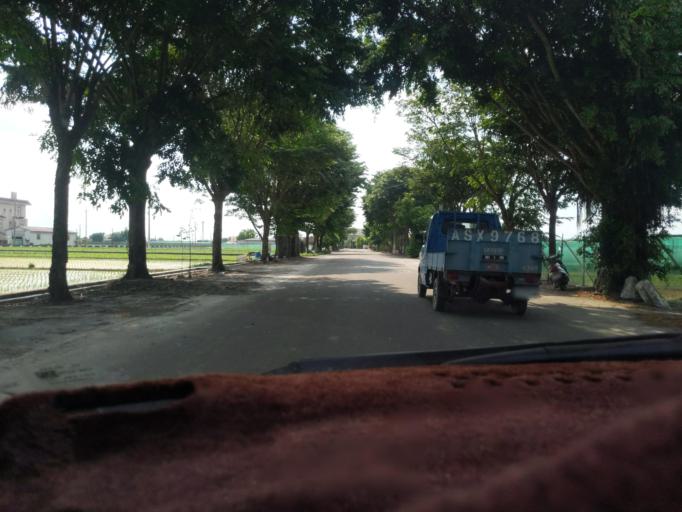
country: TW
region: Taiwan
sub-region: Yunlin
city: Douliu
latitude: 23.7880
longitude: 120.4063
